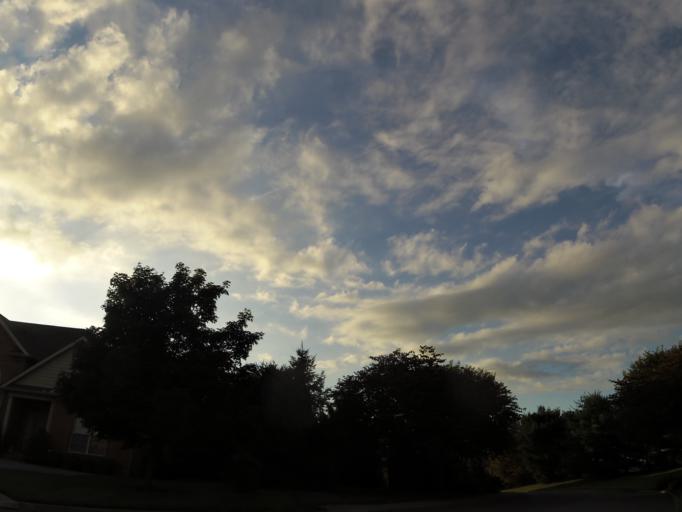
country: US
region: Tennessee
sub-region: Knox County
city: Farragut
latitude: 35.8726
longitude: -84.1614
